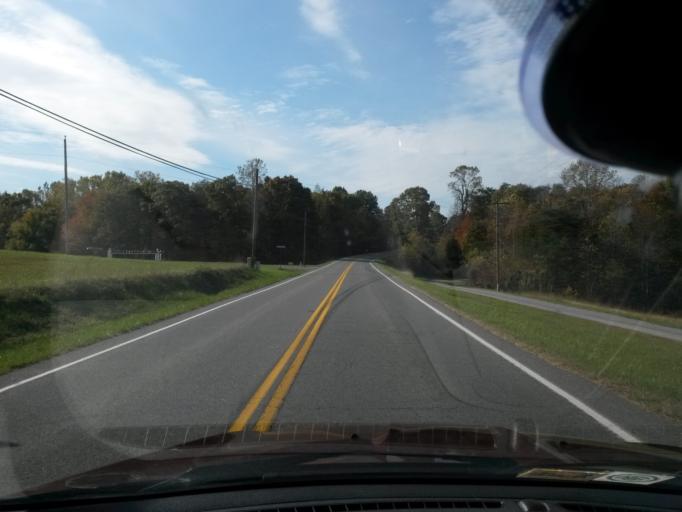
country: US
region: Virginia
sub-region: Franklin County
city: North Shore
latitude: 37.1159
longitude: -79.8009
